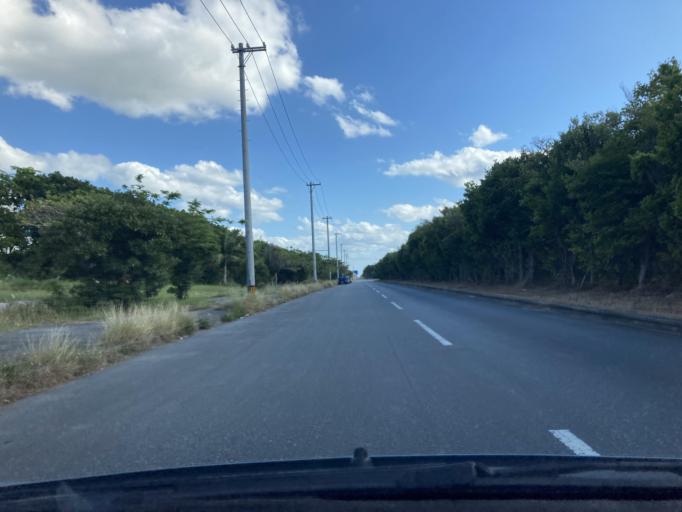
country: JP
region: Okinawa
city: Katsuren-haebaru
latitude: 26.3412
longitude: 127.8583
